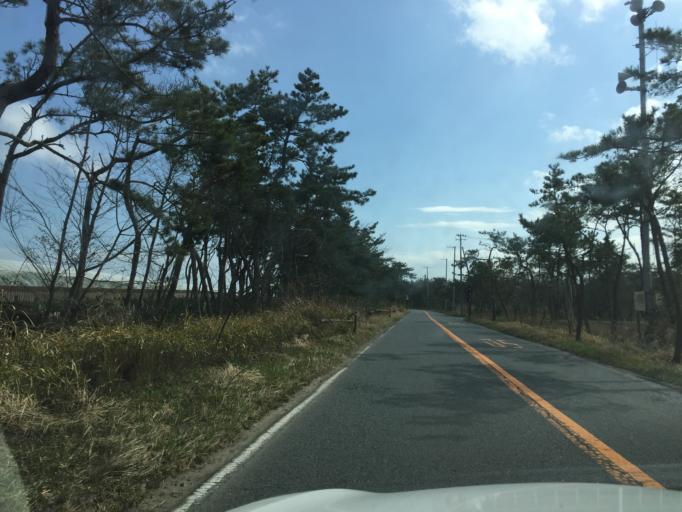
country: JP
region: Fukushima
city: Iwaki
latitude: 37.0405
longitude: 140.9720
